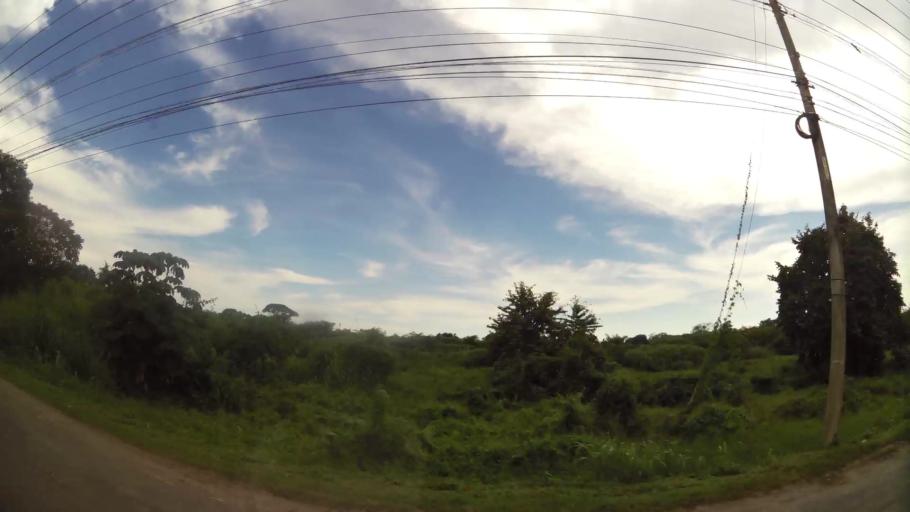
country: PA
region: Panama
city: Tocumen
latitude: 9.0692
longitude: -79.3957
